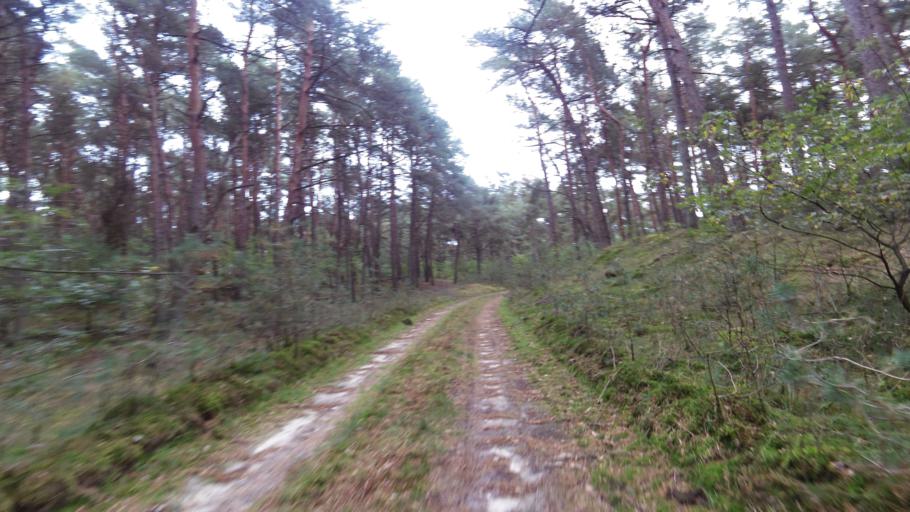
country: NL
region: Gelderland
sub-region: Gemeente Ede
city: Harskamp
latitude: 52.1647
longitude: 5.7817
